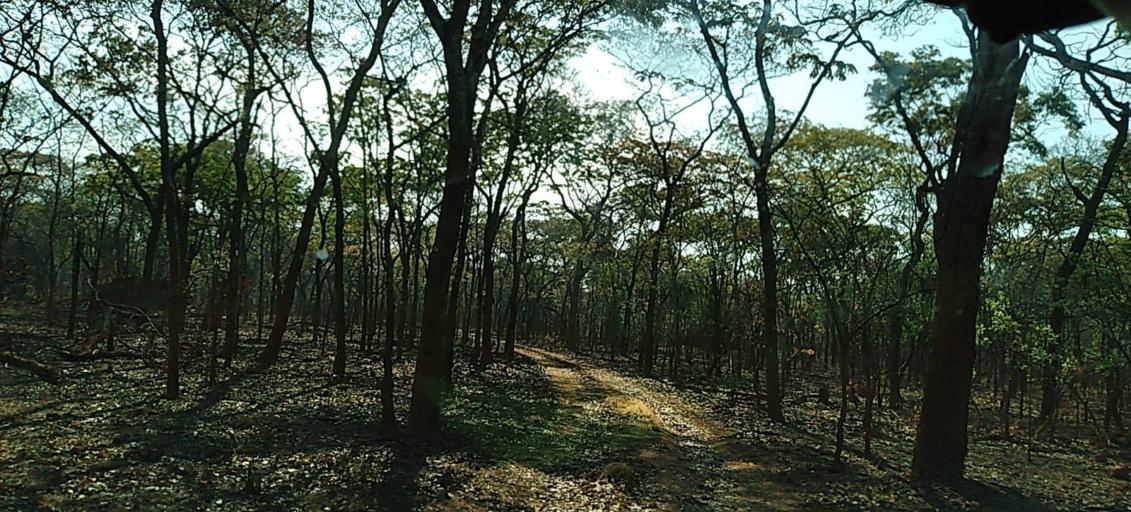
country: ZM
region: North-Western
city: Kalengwa
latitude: -13.2276
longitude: 25.0896
